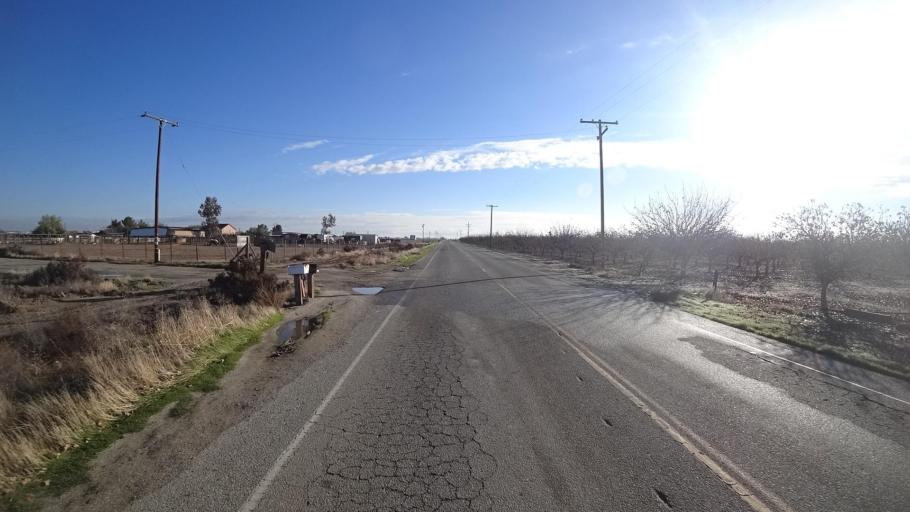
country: US
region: California
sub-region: Kern County
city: Delano
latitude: 35.7761
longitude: -119.3346
